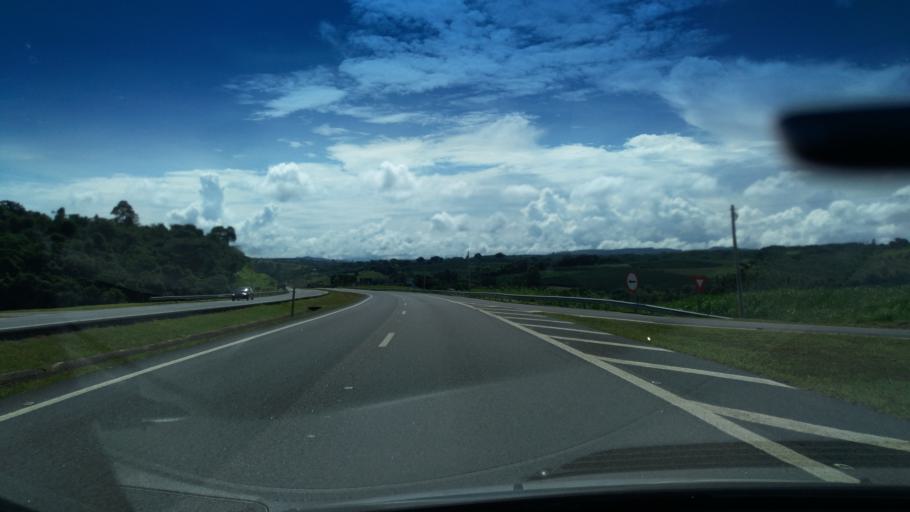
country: BR
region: Sao Paulo
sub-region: Santo Antonio Do Jardim
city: Espirito Santo do Pinhal
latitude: -22.2395
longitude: -46.8006
